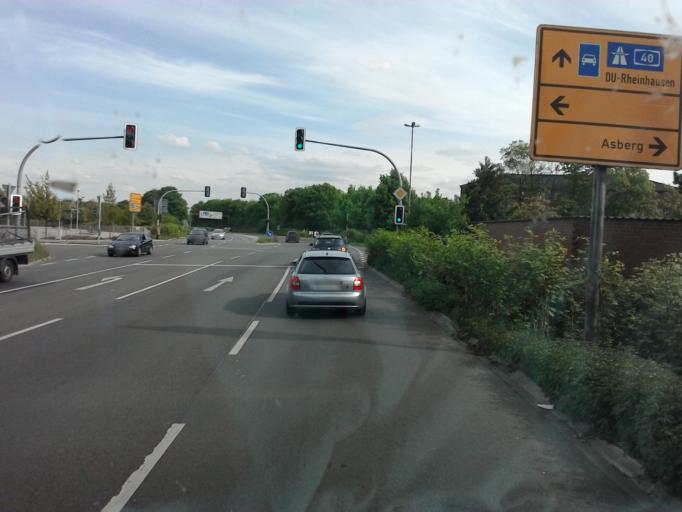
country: DE
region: North Rhine-Westphalia
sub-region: Regierungsbezirk Dusseldorf
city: Moers
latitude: 51.4430
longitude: 6.6614
